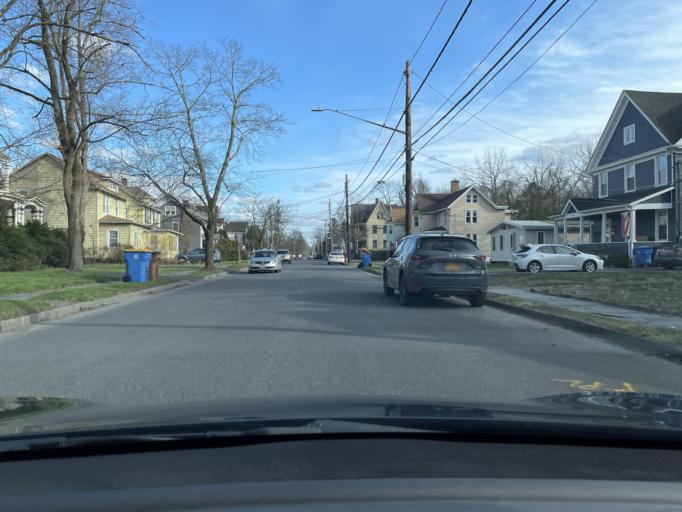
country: US
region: New York
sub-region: Ulster County
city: Kingston
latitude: 41.9295
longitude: -74.0203
